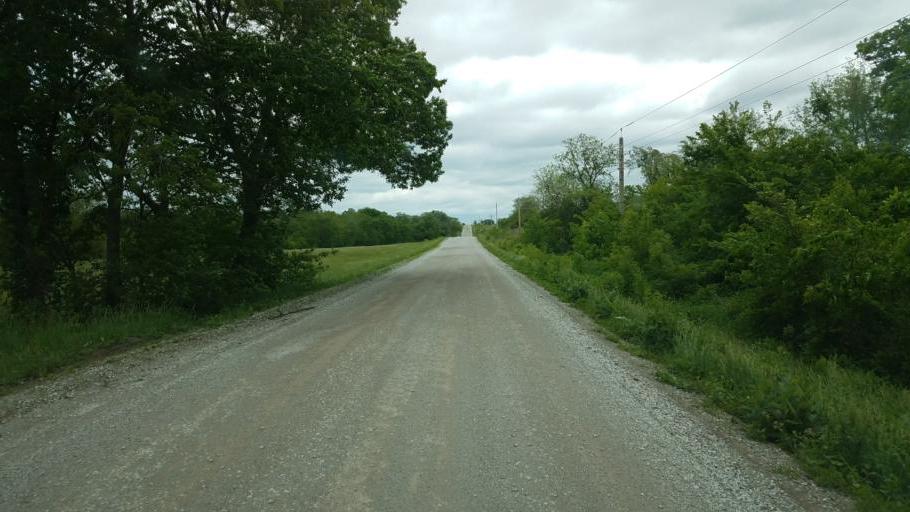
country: US
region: Iowa
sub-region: Decatur County
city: Lamoni
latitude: 40.6383
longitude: -93.8534
